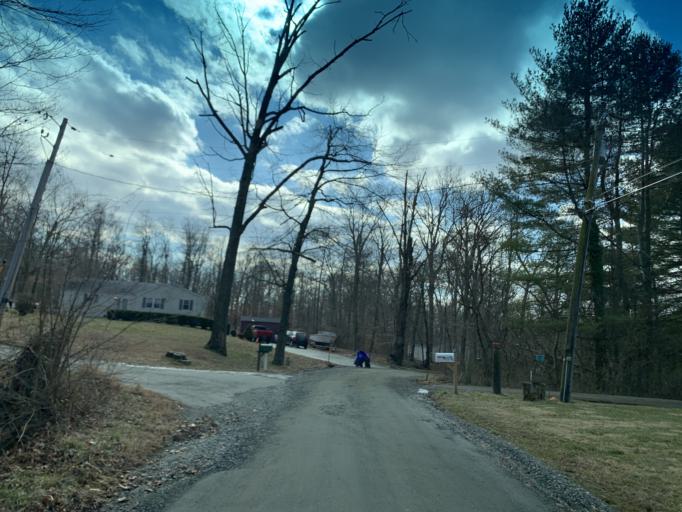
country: US
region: Maryland
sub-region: Harford County
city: Riverside
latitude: 39.5047
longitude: -76.2507
